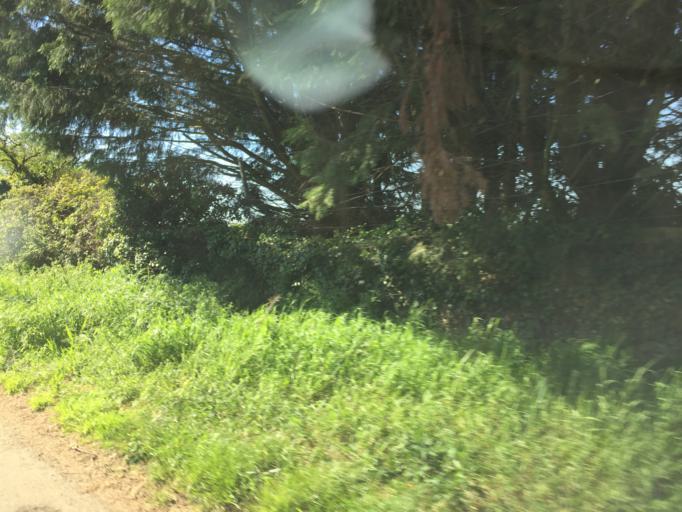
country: GB
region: England
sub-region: Wiltshire
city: Luckington
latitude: 51.5858
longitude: -2.2501
